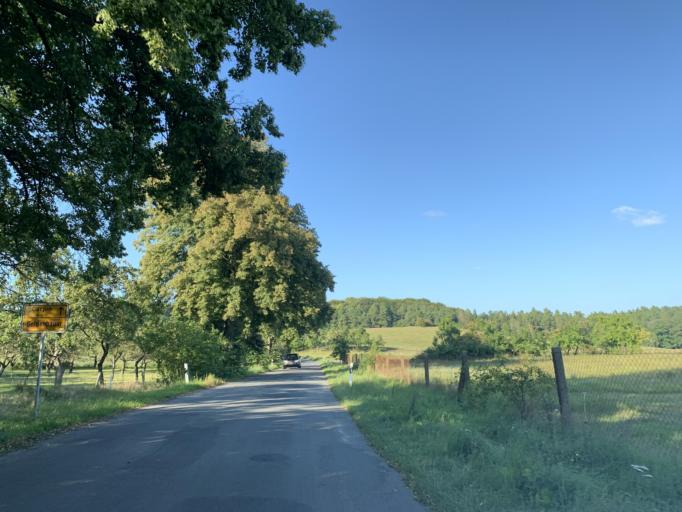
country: DE
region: Mecklenburg-Vorpommern
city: Carpin
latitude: 53.3269
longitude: 13.2392
